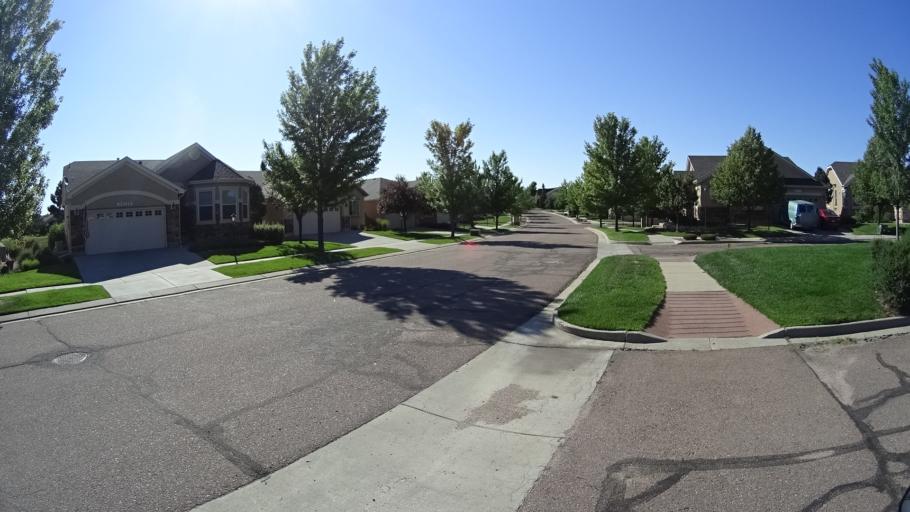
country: US
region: Colorado
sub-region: El Paso County
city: Black Forest
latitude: 38.9792
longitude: -104.7694
